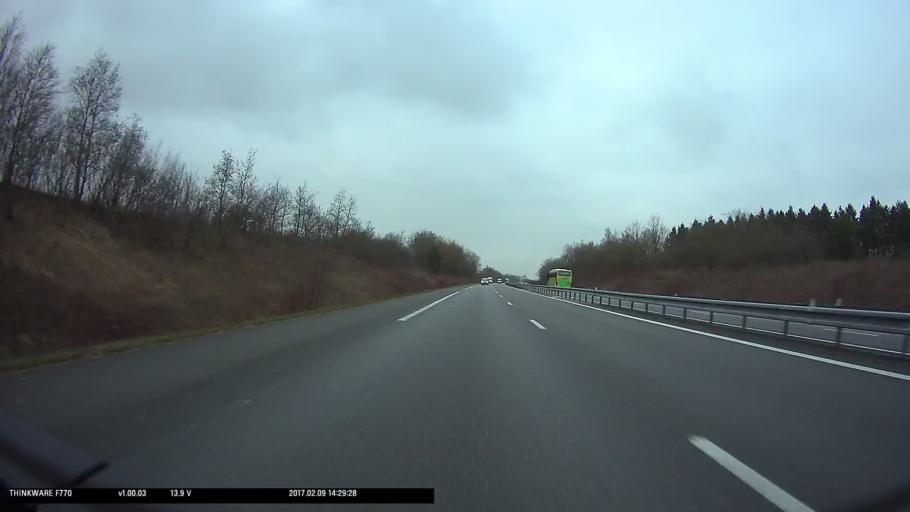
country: FR
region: Centre
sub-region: Departement du Cher
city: Mehun-sur-Yevre
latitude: 47.1140
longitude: 2.1998
